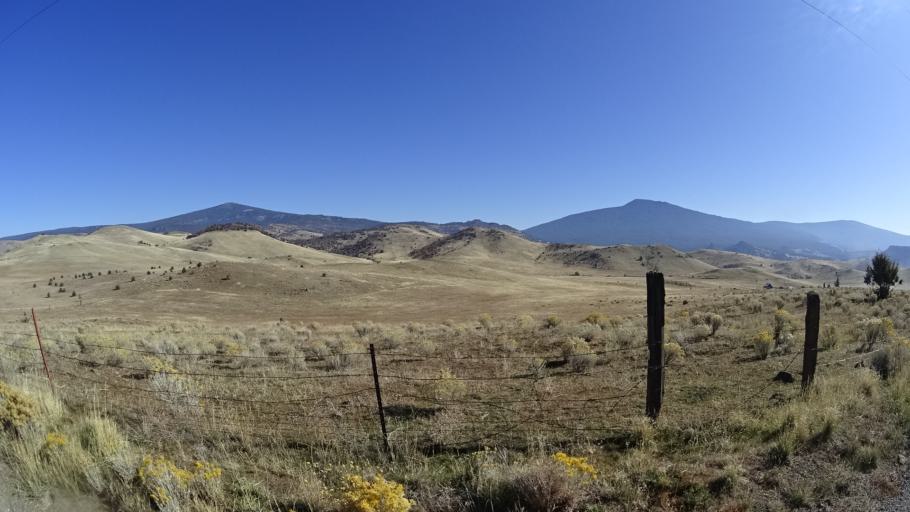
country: US
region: California
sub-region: Siskiyou County
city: Montague
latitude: 41.7702
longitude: -122.3591
